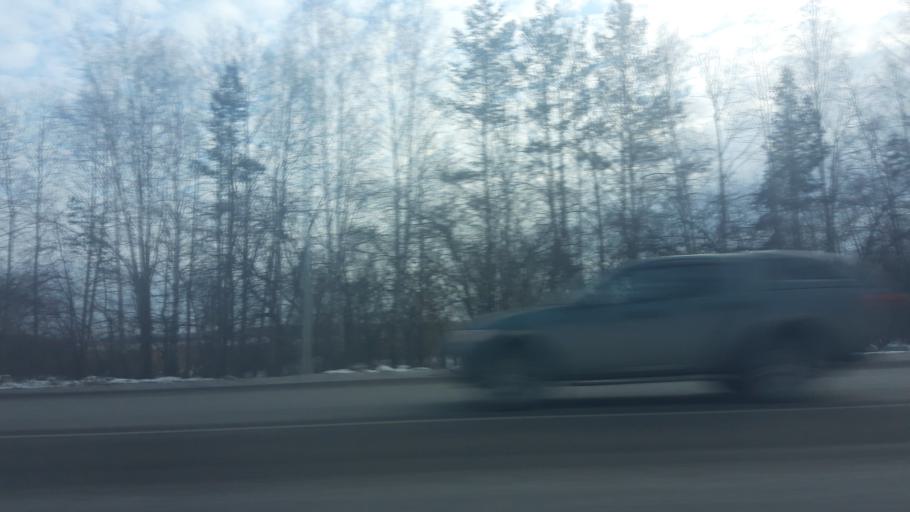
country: RU
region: Tjumen
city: Moskovskiy
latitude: 57.1854
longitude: 65.3558
